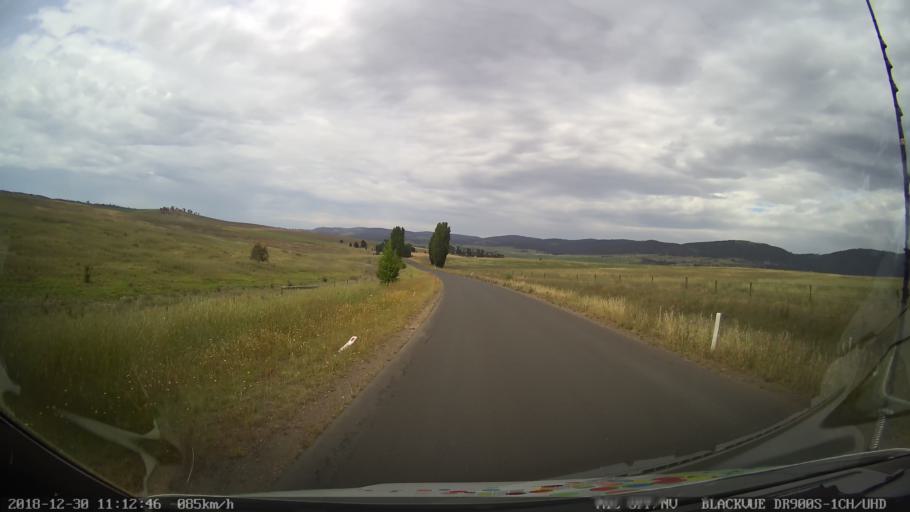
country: AU
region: New South Wales
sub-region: Snowy River
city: Jindabyne
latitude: -36.5302
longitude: 148.7522
